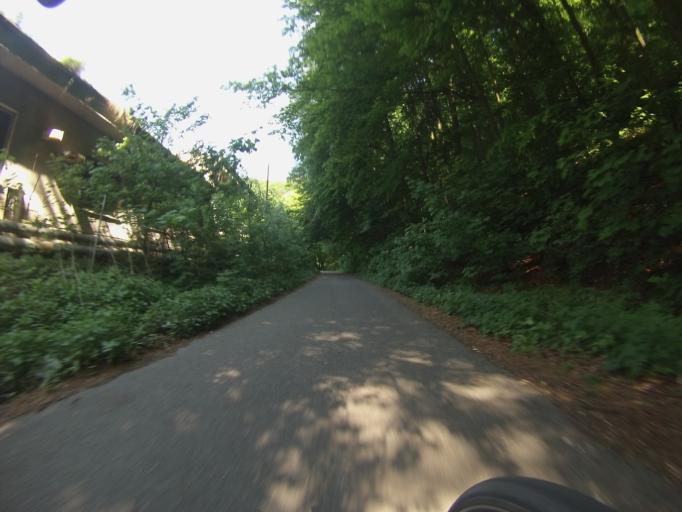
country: CZ
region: South Moravian
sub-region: Okres Blansko
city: Adamov
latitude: 49.3083
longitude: 16.6429
